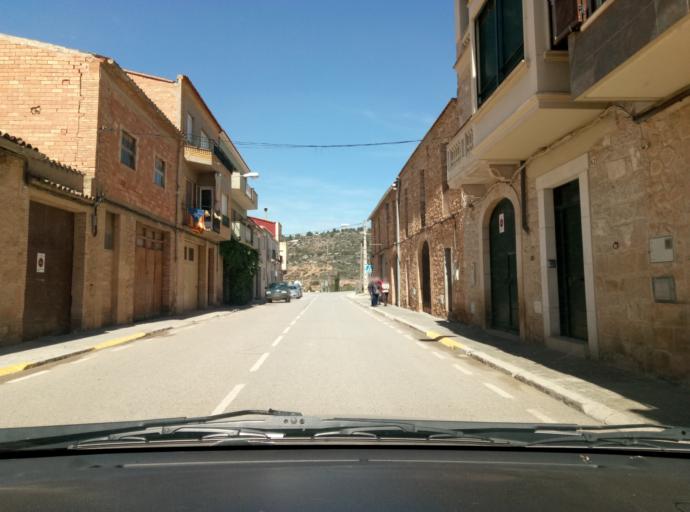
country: ES
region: Catalonia
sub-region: Provincia de Lleida
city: Juncosa
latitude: 41.4262
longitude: 0.8606
